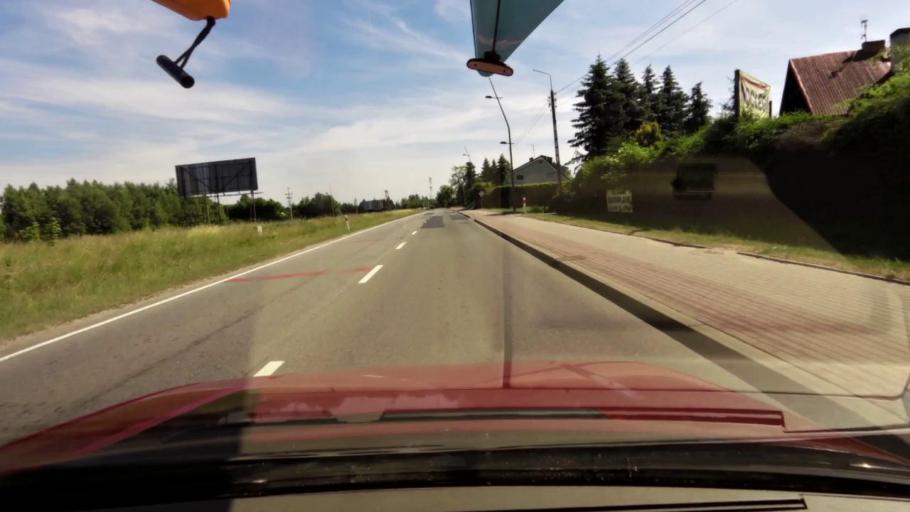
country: PL
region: Pomeranian Voivodeship
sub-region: Powiat slupski
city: Kobylnica
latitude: 54.4361
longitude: 16.9984
